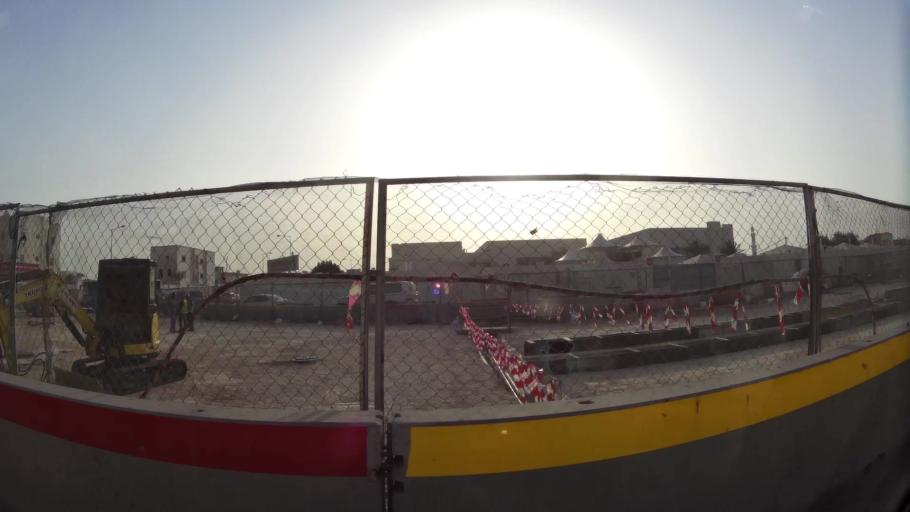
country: QA
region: Baladiyat ar Rayyan
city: Ar Rayyan
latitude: 25.2524
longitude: 51.4508
